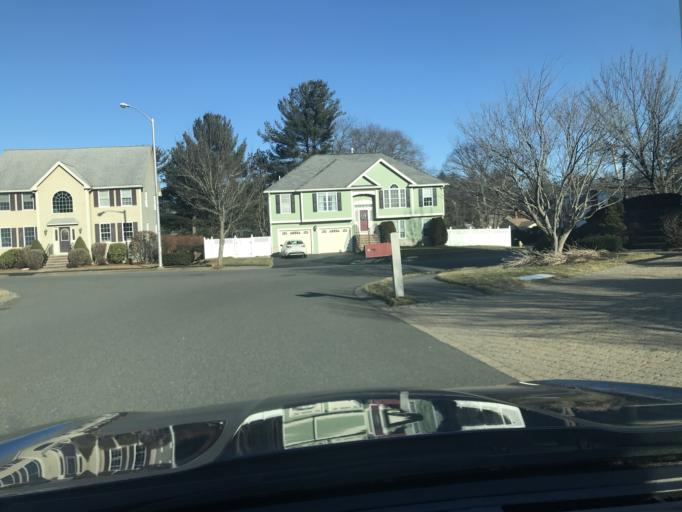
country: US
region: Massachusetts
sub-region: Essex County
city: Saugus
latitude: 42.4852
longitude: -71.0104
